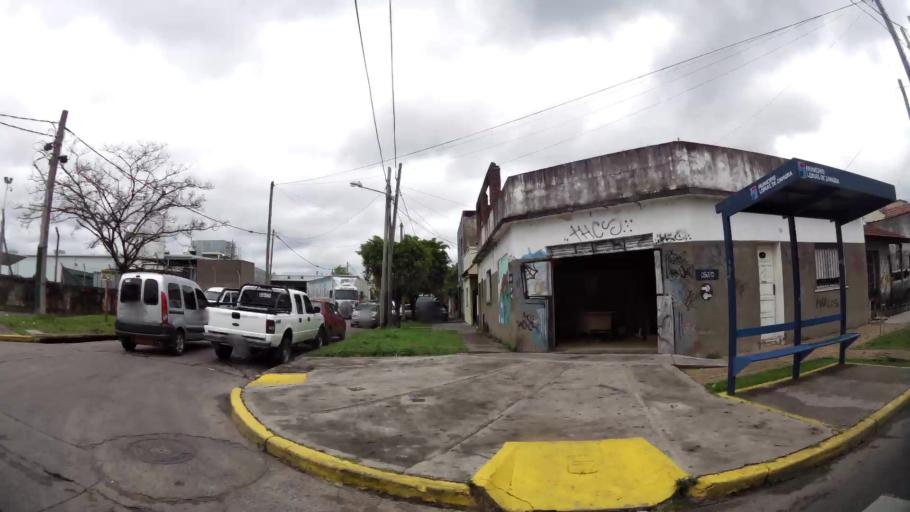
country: AR
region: Buenos Aires
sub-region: Partido de Lomas de Zamora
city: Lomas de Zamora
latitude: -34.7573
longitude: -58.3788
